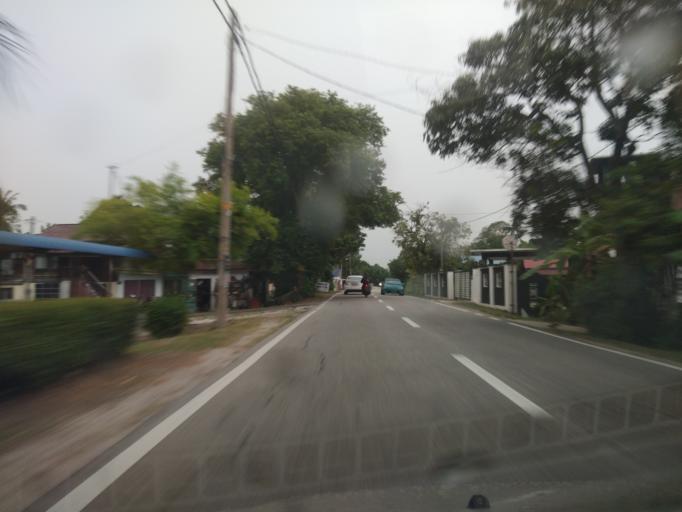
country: MY
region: Penang
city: Permatang Kuching
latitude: 5.4853
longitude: 100.4007
